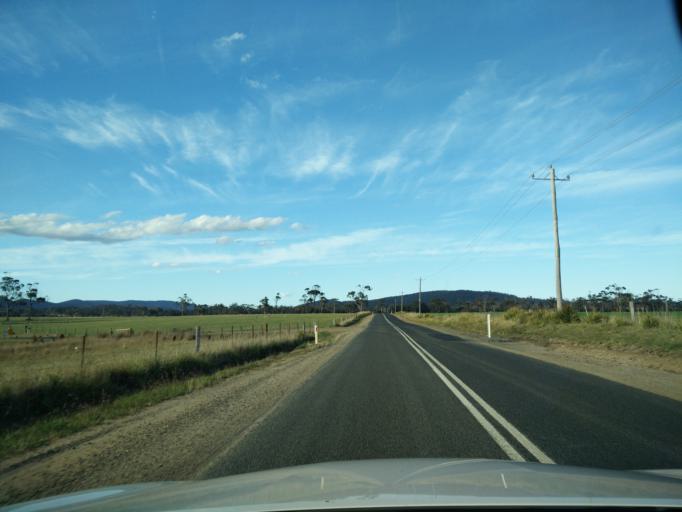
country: AU
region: Tasmania
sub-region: Break O'Day
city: St Helens
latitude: -41.9087
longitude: 148.2526
